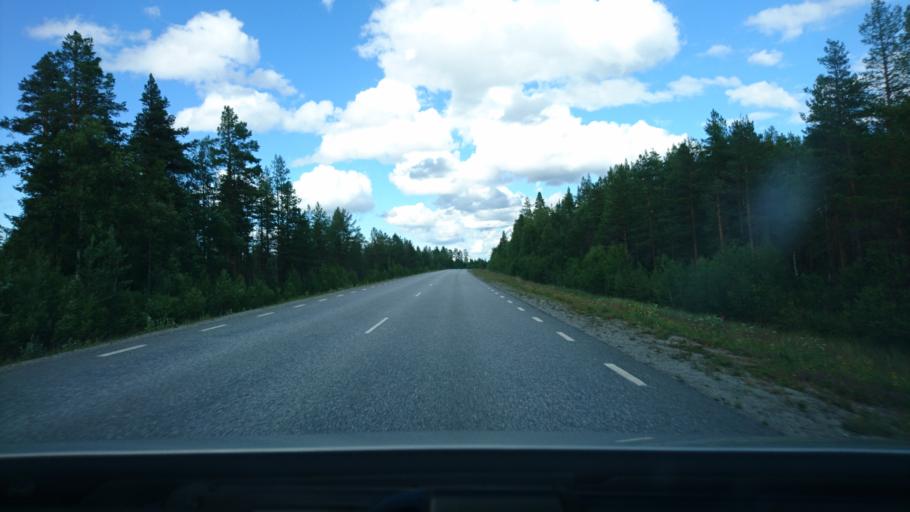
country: SE
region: Vaesterbotten
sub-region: Asele Kommun
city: Asele
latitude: 64.1395
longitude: 17.3311
